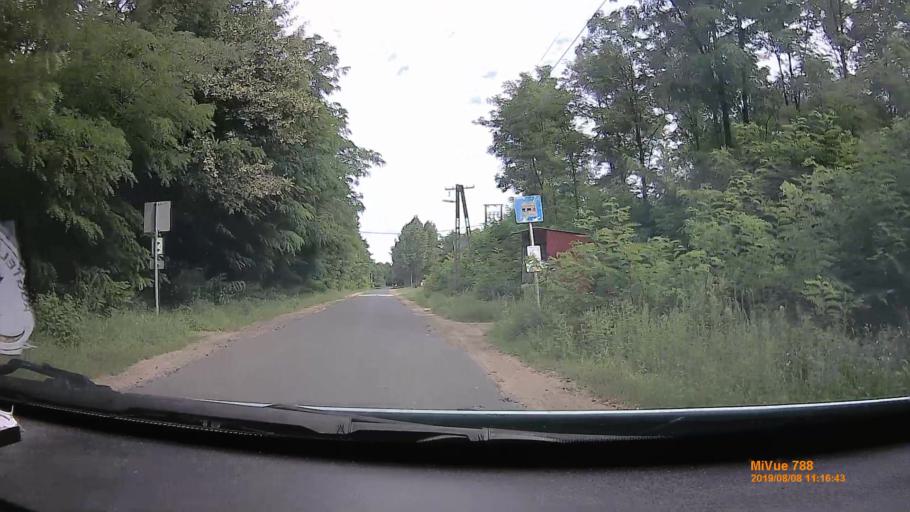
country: HU
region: Szabolcs-Szatmar-Bereg
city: Balkany
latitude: 47.7259
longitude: 21.8294
